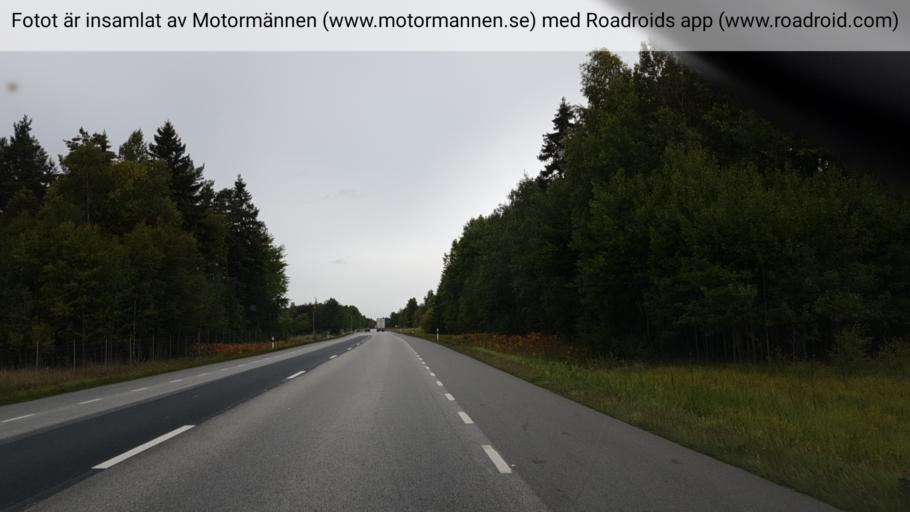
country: SE
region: Vaestra Goetaland
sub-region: Mariestads Kommun
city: Mariestad
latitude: 58.6534
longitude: 13.7405
